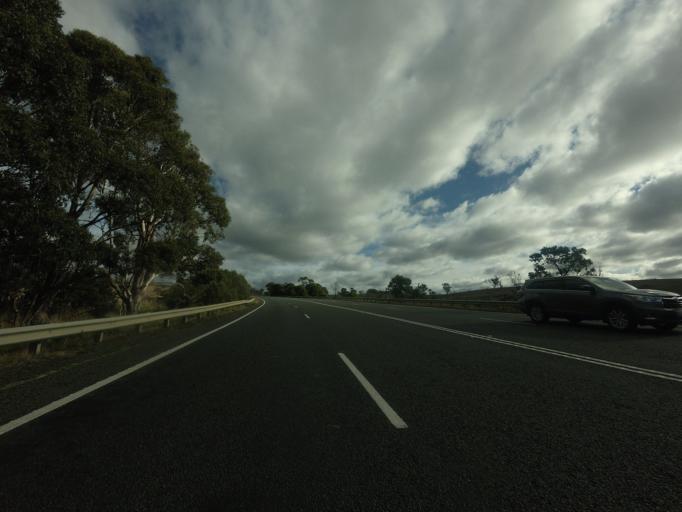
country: AU
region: Tasmania
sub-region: Brighton
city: Bridgewater
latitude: -42.4458
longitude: 147.2167
